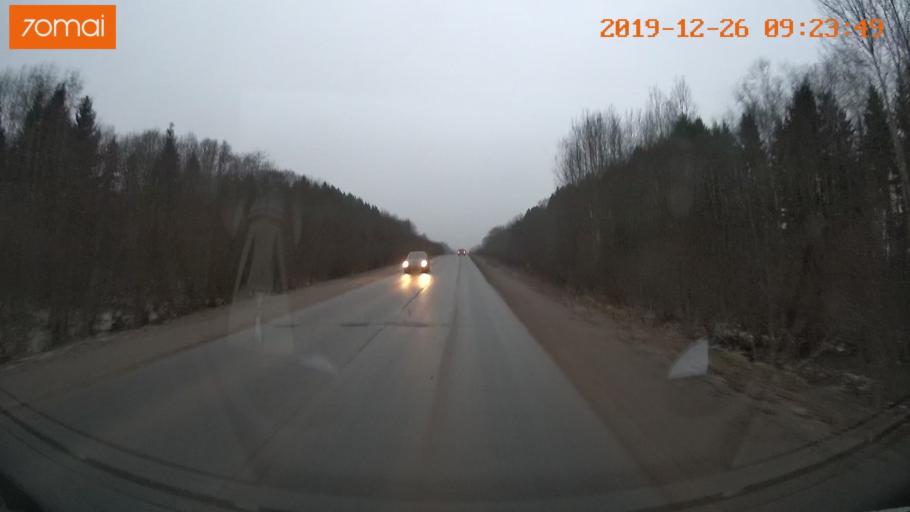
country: RU
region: Vologda
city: Gryazovets
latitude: 58.9933
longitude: 40.2058
